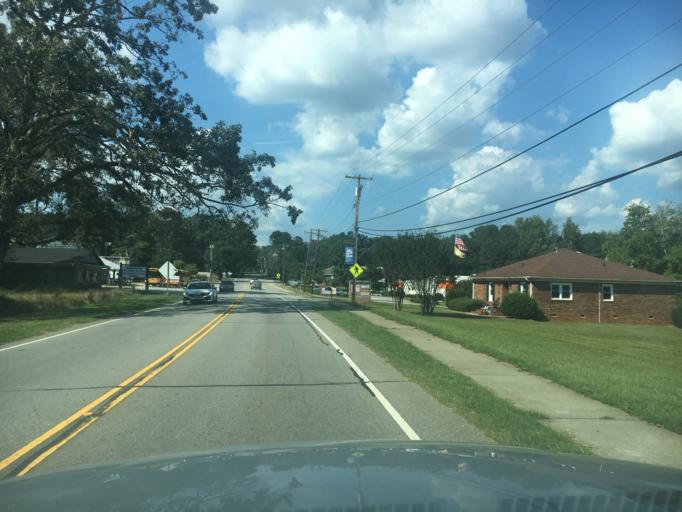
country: US
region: South Carolina
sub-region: Anderson County
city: Pendleton
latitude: 34.6409
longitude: -82.7819
